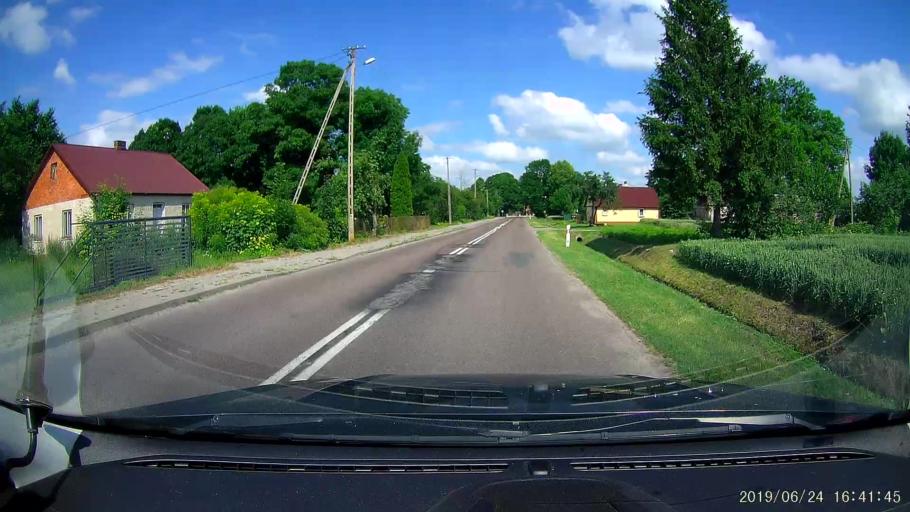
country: PL
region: Lublin Voivodeship
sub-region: Powiat tomaszowski
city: Michalow
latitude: 50.5345
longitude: 23.6057
